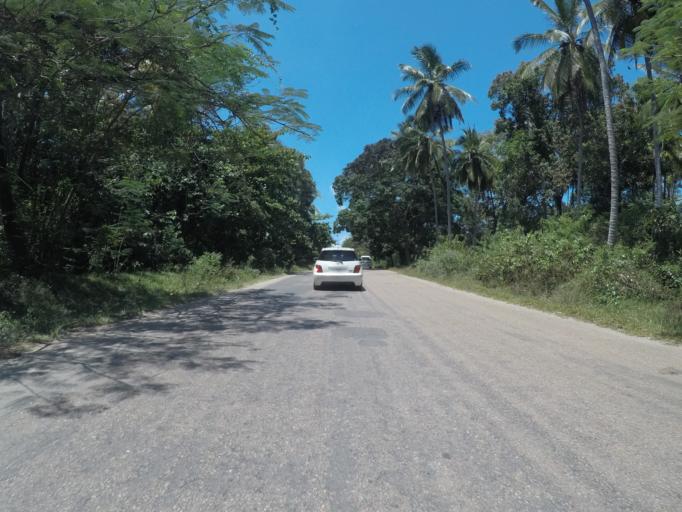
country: TZ
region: Zanzibar Central/South
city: Koani
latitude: -6.2018
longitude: 39.3211
